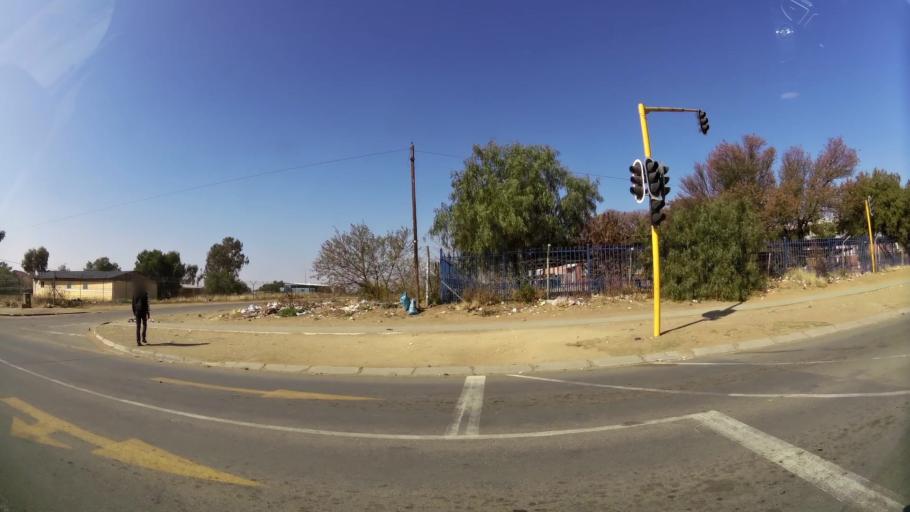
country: ZA
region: Orange Free State
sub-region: Mangaung Metropolitan Municipality
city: Bloemfontein
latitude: -29.1570
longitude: 26.2473
